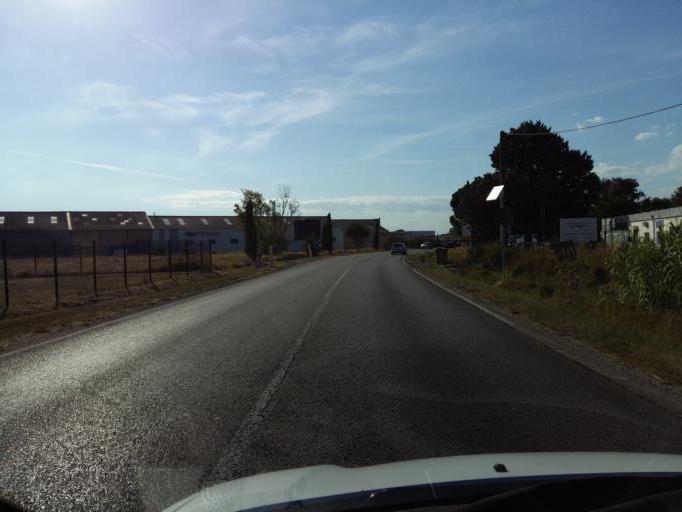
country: FR
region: Provence-Alpes-Cote d'Azur
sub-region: Departement du Vaucluse
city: Le Thor
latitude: 43.9220
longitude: 5.0139
